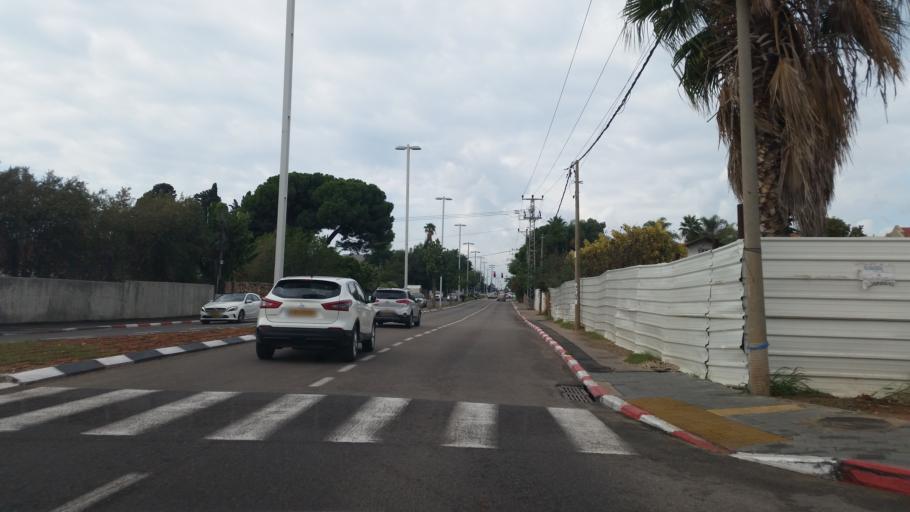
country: IL
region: Tel Aviv
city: Kefar Shemaryahu
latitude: 32.1794
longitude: 34.8217
